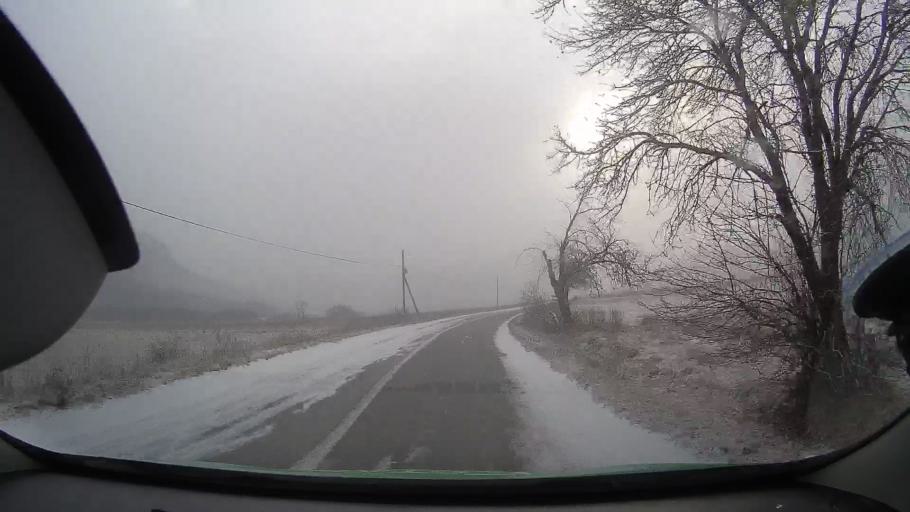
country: RO
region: Alba
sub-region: Comuna Rimetea
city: Rimetea
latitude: 46.4017
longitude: 23.5582
